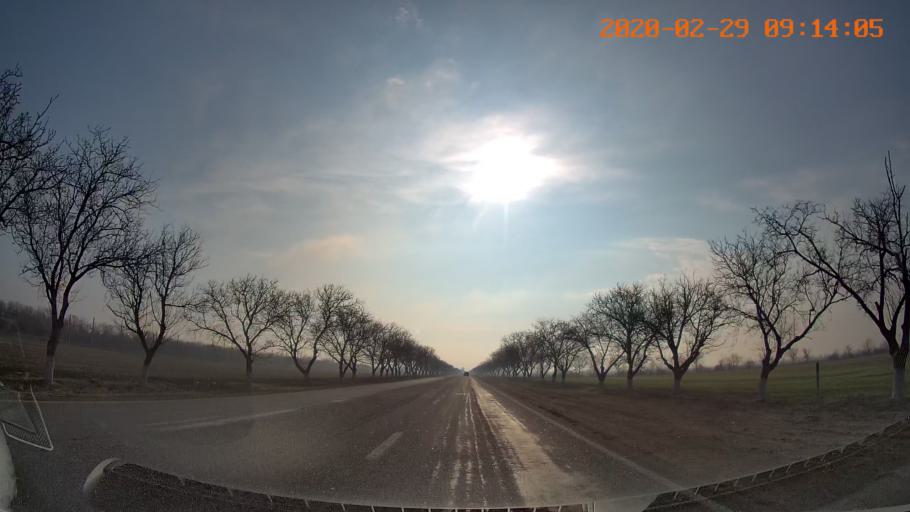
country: MD
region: Telenesti
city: Pervomaisc
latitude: 46.8117
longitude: 29.8467
